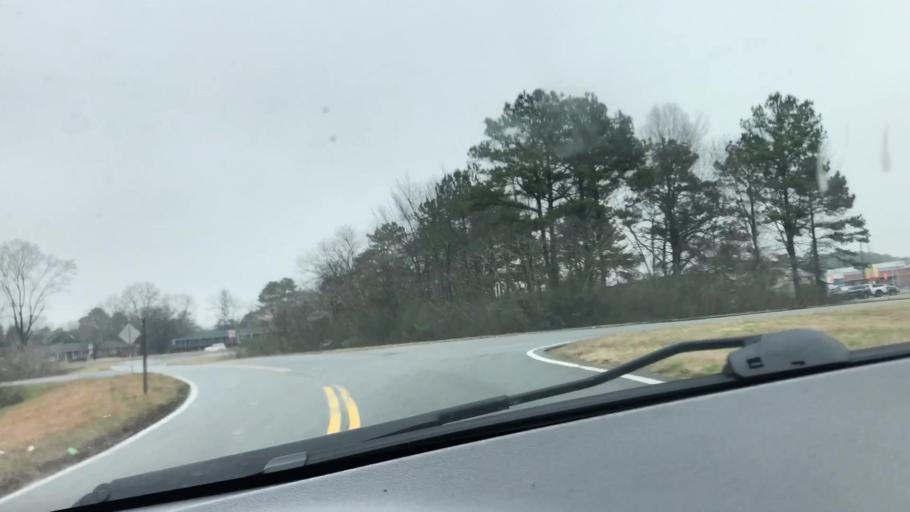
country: US
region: Georgia
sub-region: Bartow County
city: Cartersville
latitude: 34.2062
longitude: -84.8219
